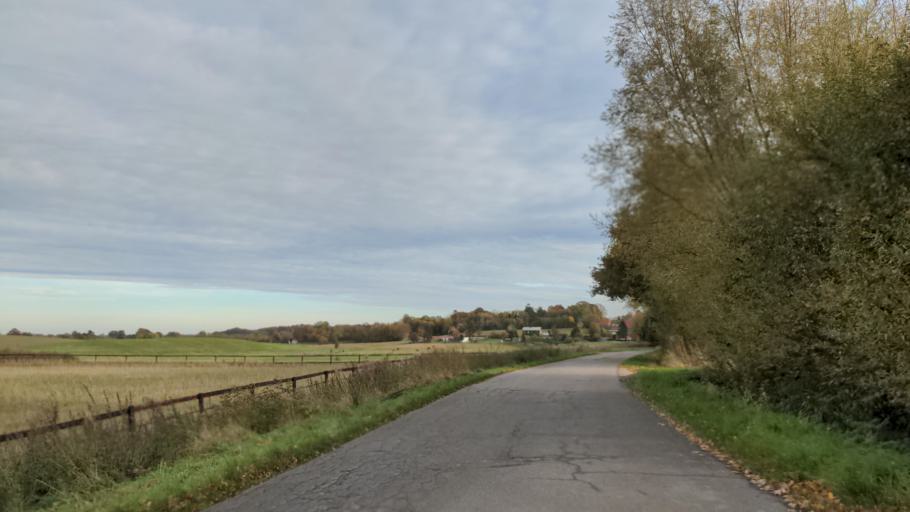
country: DE
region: Schleswig-Holstein
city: Bosdorf
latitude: 54.1138
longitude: 10.5348
